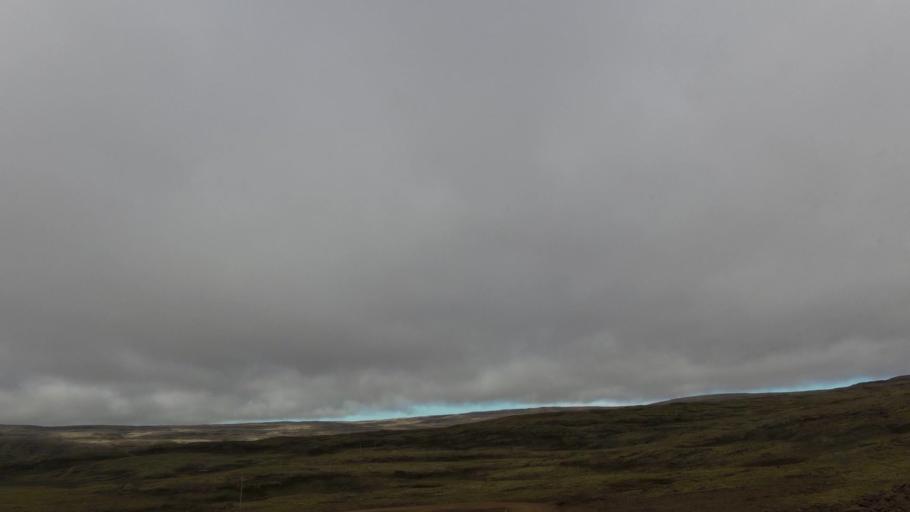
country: IS
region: West
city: Olafsvik
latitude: 65.5376
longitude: -24.3592
